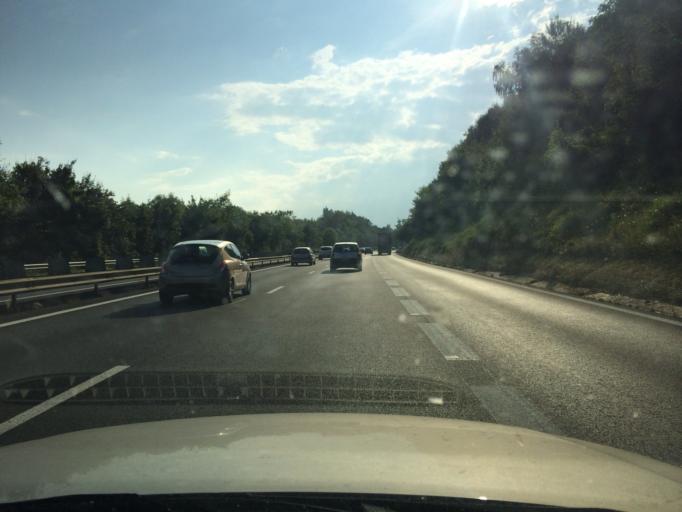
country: FR
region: Lower Normandy
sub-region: Departement du Calvados
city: Saint-Gatien-des-Bois
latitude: 49.2640
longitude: 0.1594
